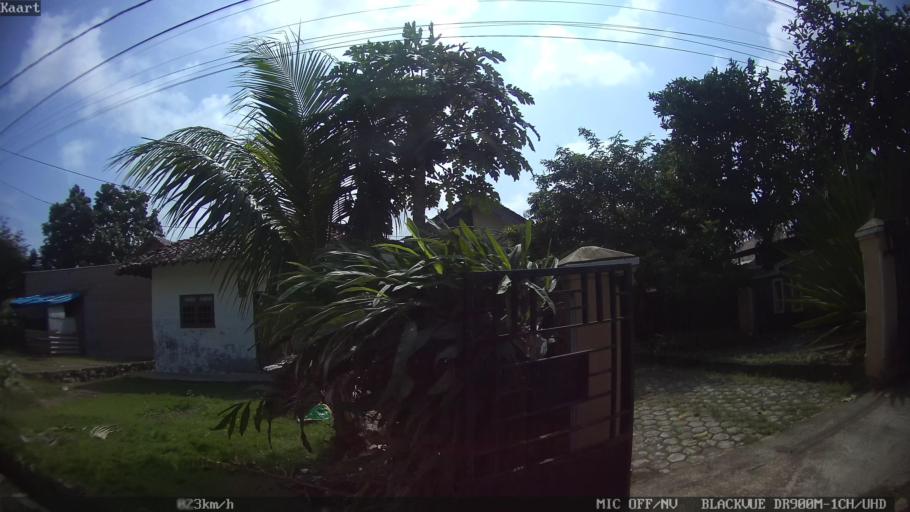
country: ID
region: Lampung
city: Kedaton
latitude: -5.3483
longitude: 105.2892
